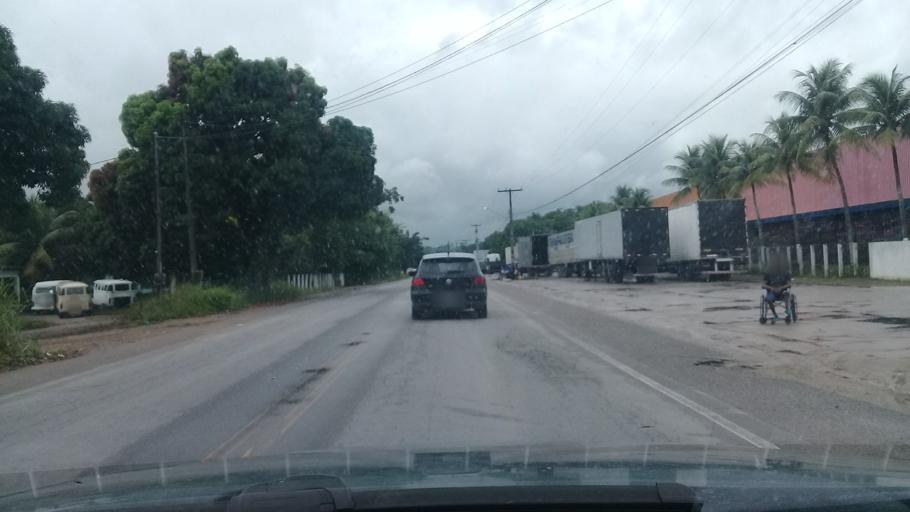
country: BR
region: Pernambuco
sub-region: Igarassu
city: Igarassu
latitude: -7.8211
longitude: -34.9111
